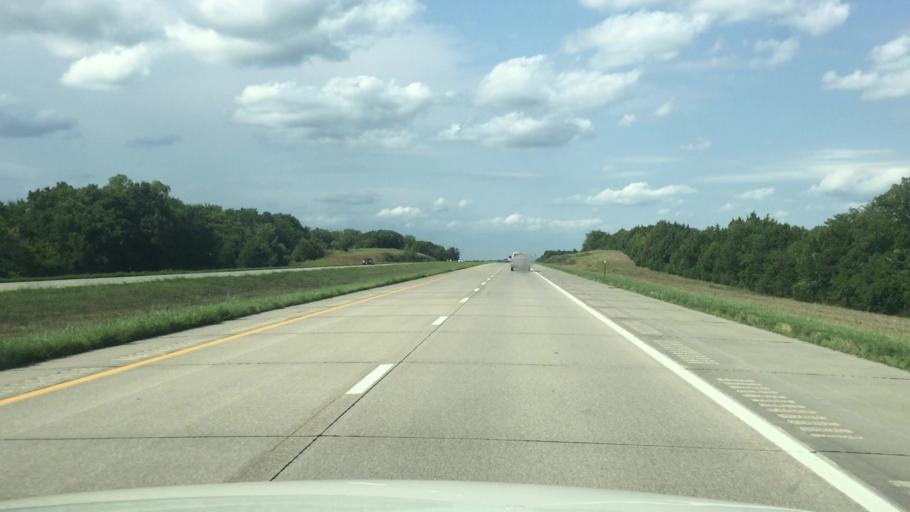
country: US
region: Kansas
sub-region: Miami County
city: Louisburg
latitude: 38.5804
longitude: -94.6954
